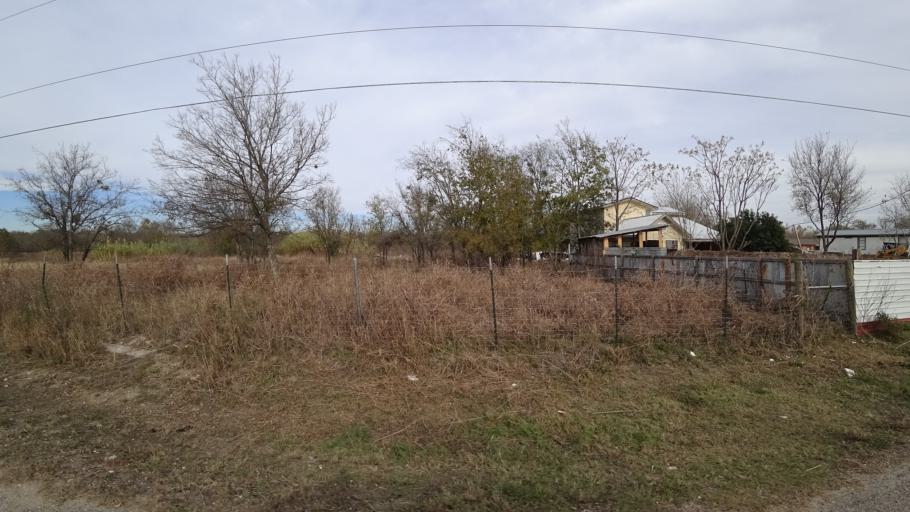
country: US
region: Texas
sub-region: Travis County
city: Garfield
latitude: 30.1249
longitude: -97.6170
